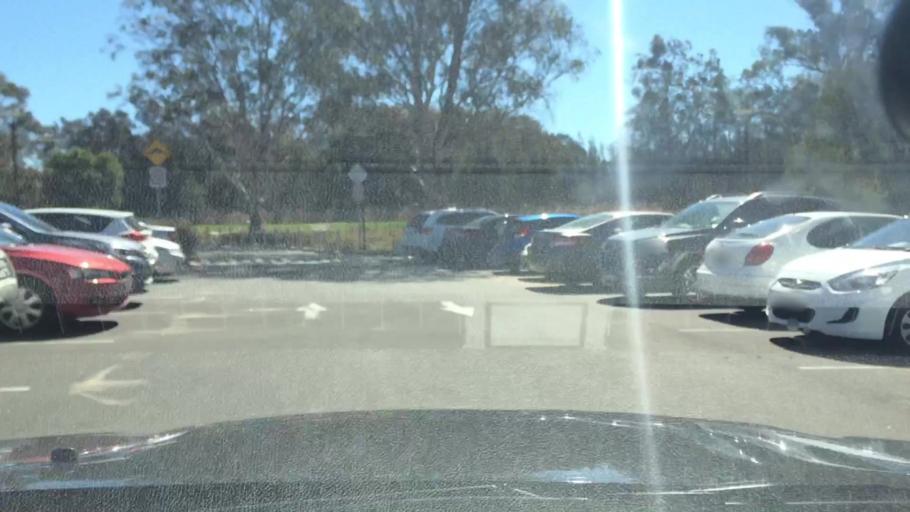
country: AU
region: New South Wales
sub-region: Liverpool
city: Miller
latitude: -33.9348
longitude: 150.8467
